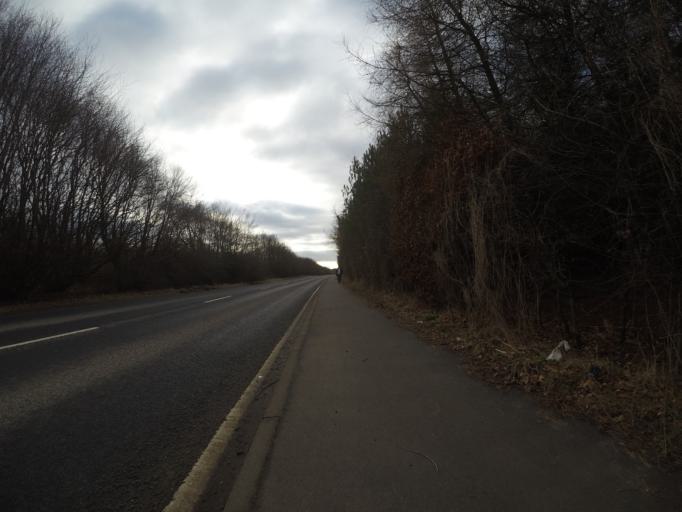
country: GB
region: Scotland
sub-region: North Ayrshire
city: Irvine
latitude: 55.5906
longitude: -4.6508
